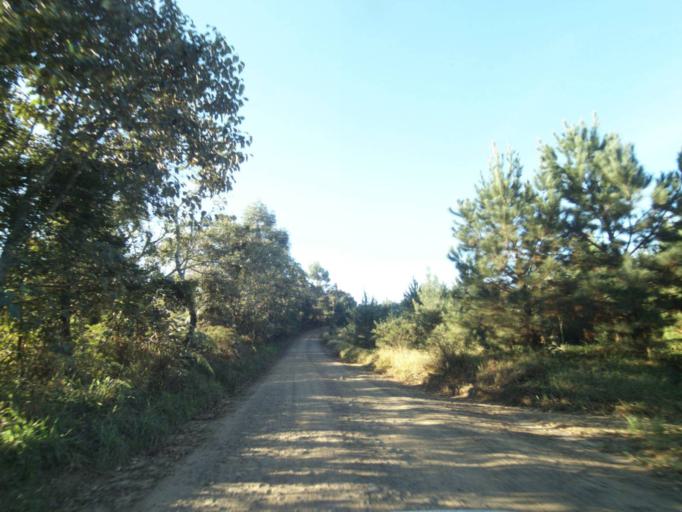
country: BR
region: Parana
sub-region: Tibagi
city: Tibagi
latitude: -24.5268
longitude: -50.5932
